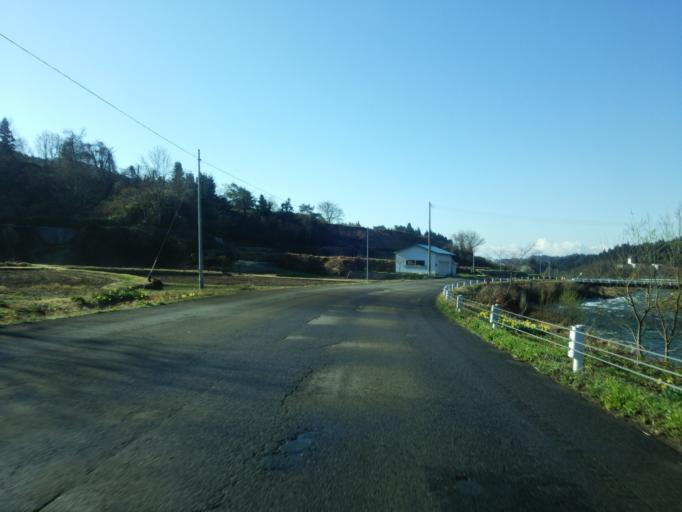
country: JP
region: Fukushima
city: Kitakata
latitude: 37.7241
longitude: 139.7803
